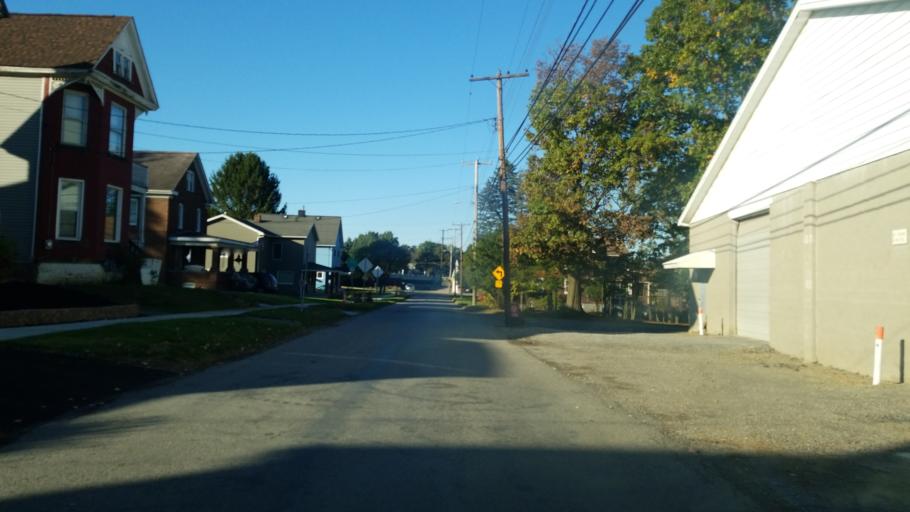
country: US
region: Pennsylvania
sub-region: Jefferson County
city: Punxsutawney
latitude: 40.9381
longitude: -78.9742
